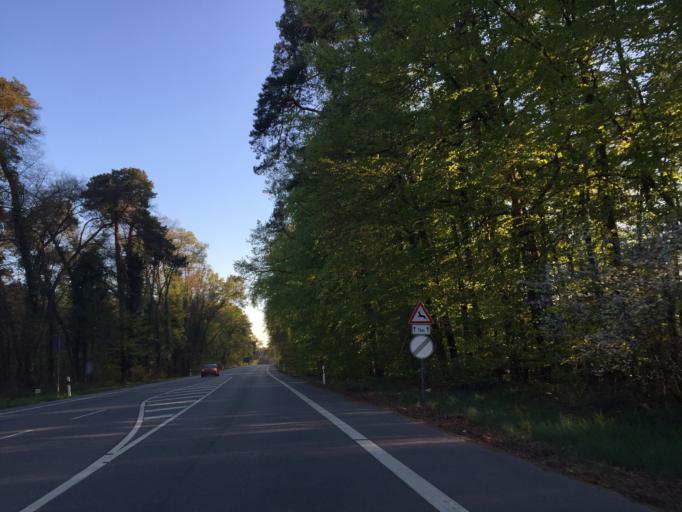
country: DE
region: Hesse
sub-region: Regierungsbezirk Darmstadt
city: Bickenbach
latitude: 49.7677
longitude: 8.6233
